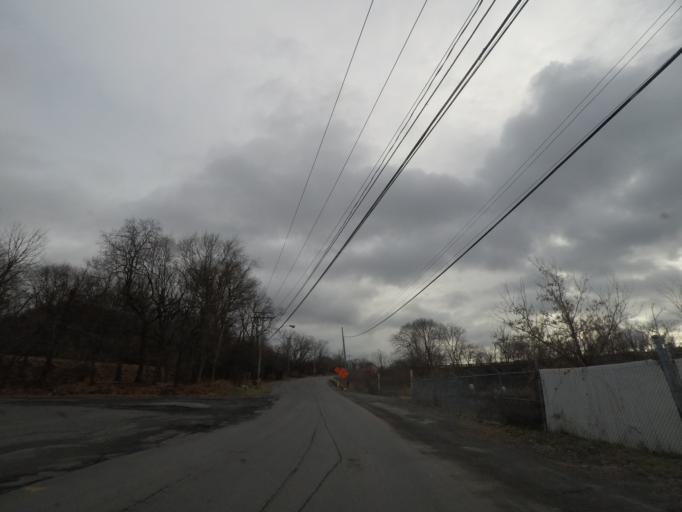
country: US
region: New York
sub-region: Rensselaer County
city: Rensselaer
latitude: 42.6316
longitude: -73.7433
